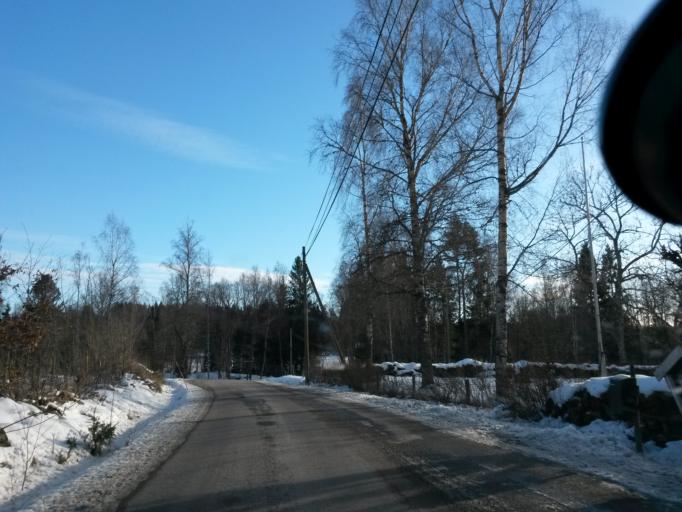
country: SE
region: Vaestra Goetaland
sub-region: Vargarda Kommun
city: Vargarda
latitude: 58.0160
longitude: 12.8911
